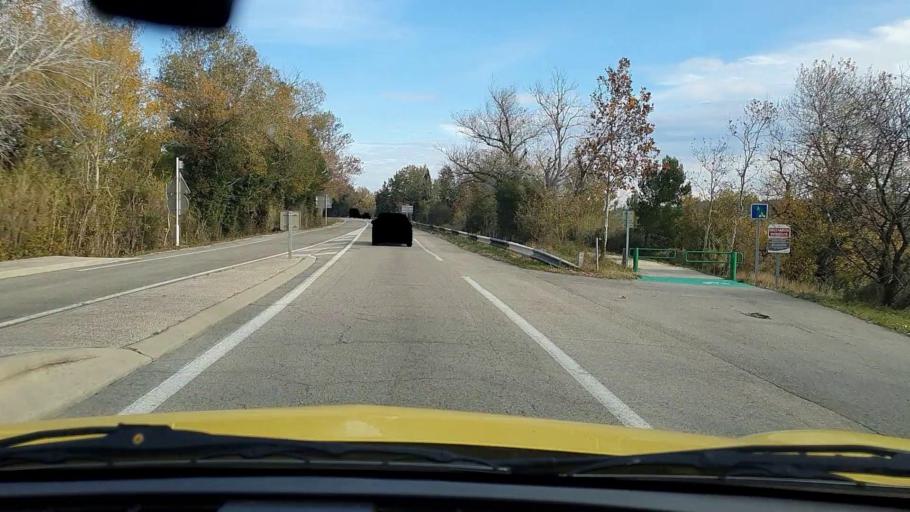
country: FR
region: Languedoc-Roussillon
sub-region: Departement du Gard
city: Aramon
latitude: 43.8867
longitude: 4.6837
